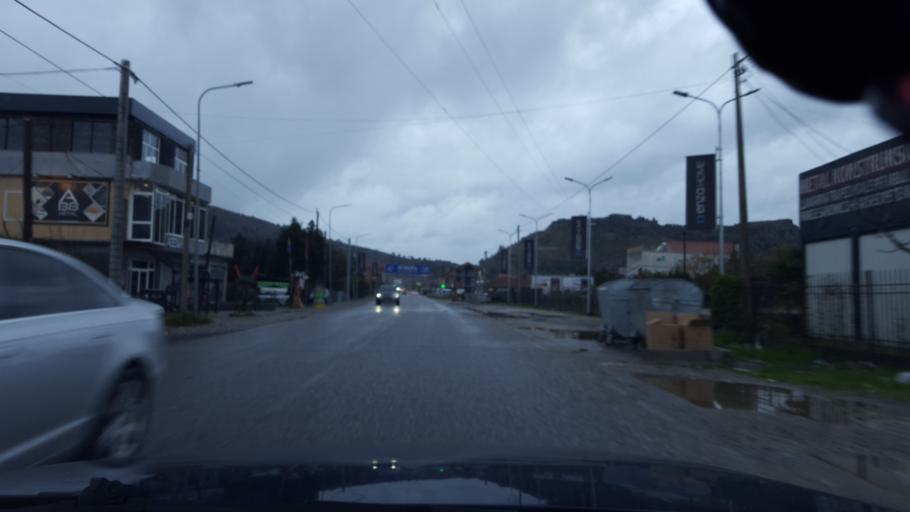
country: AL
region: Shkoder
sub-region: Rrethi i Malesia e Madhe
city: Kuc
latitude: 42.0377
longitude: 19.4981
